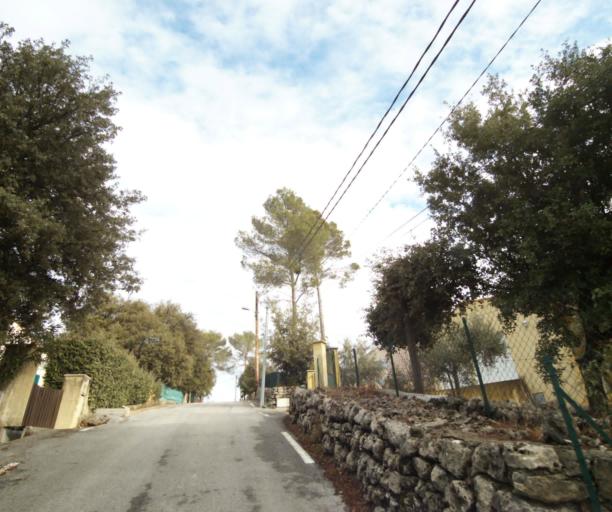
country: FR
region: Provence-Alpes-Cote d'Azur
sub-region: Departement du Var
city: Trans-en-Provence
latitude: 43.5050
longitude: 6.4966
